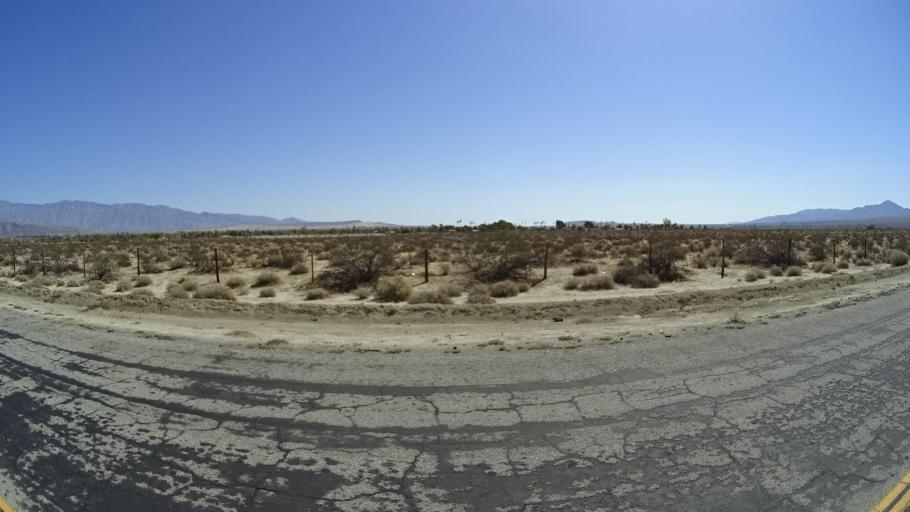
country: US
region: California
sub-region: San Diego County
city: Borrego Springs
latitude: 33.2345
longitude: -116.3656
